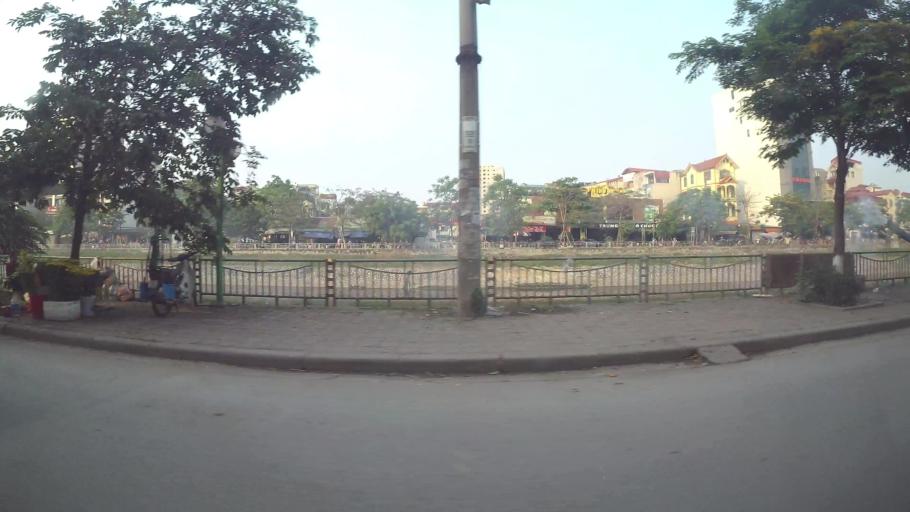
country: VN
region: Ha Noi
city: Thanh Xuan
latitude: 20.9808
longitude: 105.8178
